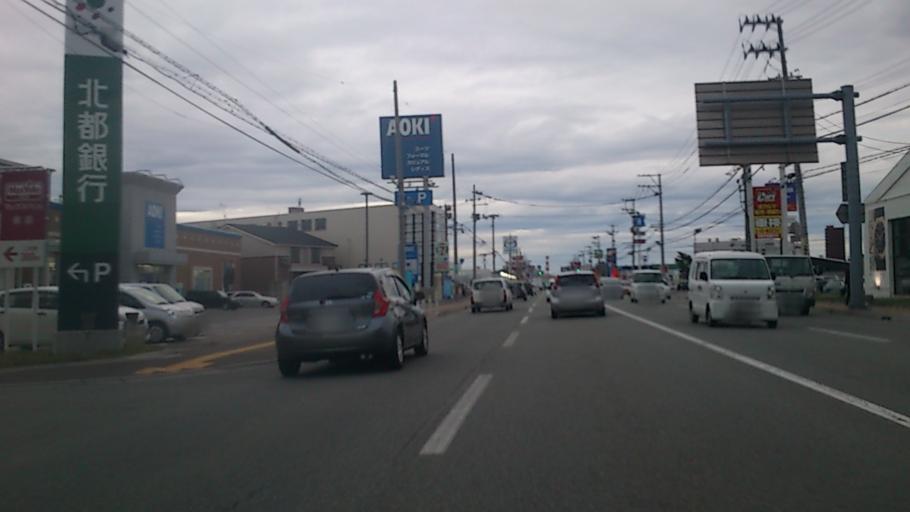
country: JP
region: Akita
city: Akita Shi
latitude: 39.7361
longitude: 140.0986
